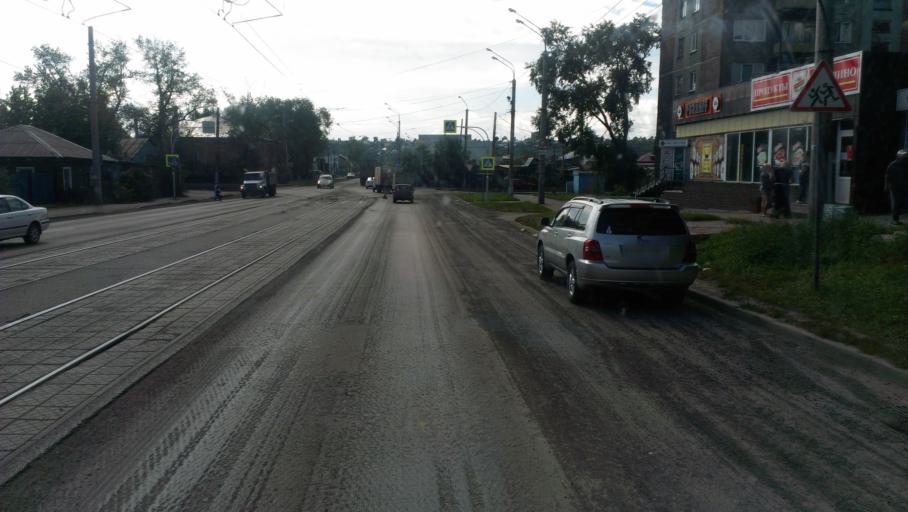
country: RU
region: Altai Krai
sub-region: Gorod Barnaulskiy
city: Barnaul
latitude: 53.3277
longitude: 83.7626
